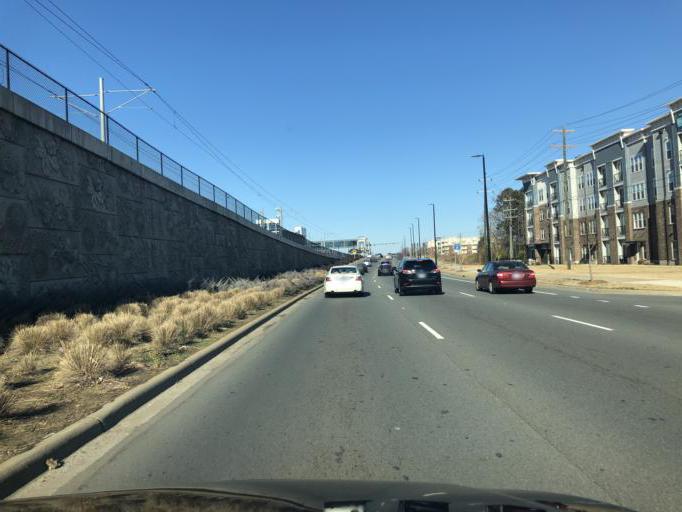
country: US
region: North Carolina
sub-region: Mecklenburg County
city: Charlotte
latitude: 35.2845
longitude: -80.7630
